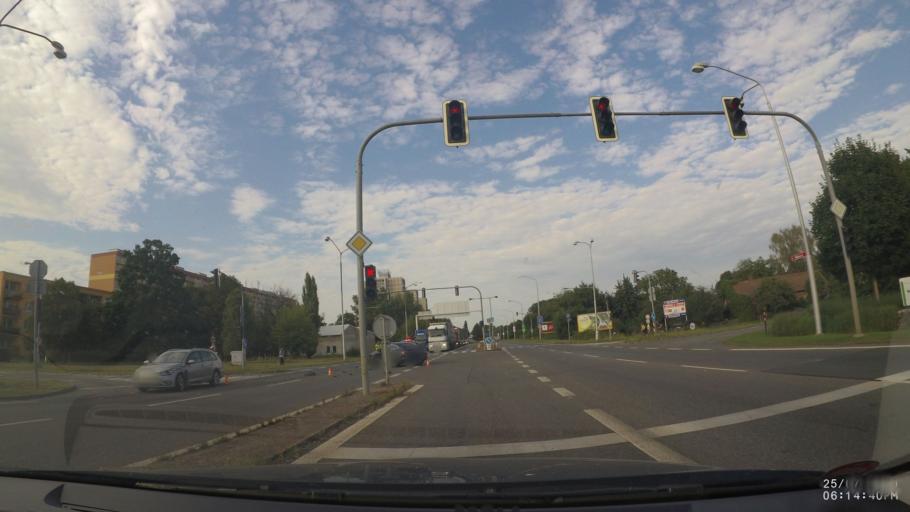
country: CZ
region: Kralovehradecky
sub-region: Okres Hradec Kralove
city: Hradec Kralove
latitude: 50.1963
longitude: 15.8137
